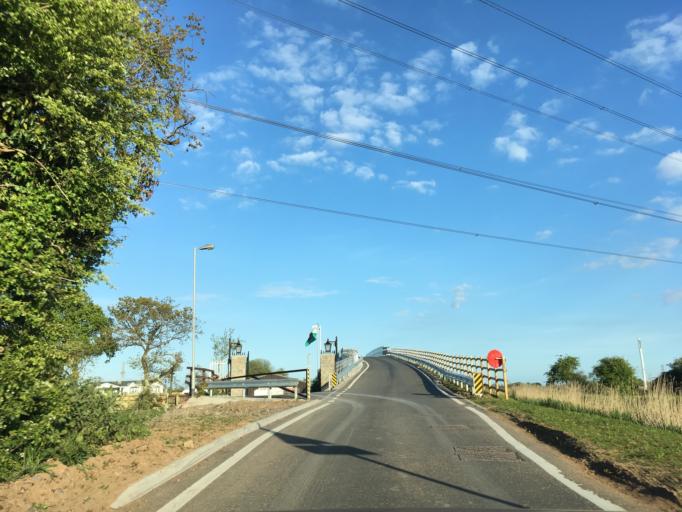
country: GB
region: Wales
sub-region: Newport
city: Marshfield
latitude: 51.5233
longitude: -3.0762
